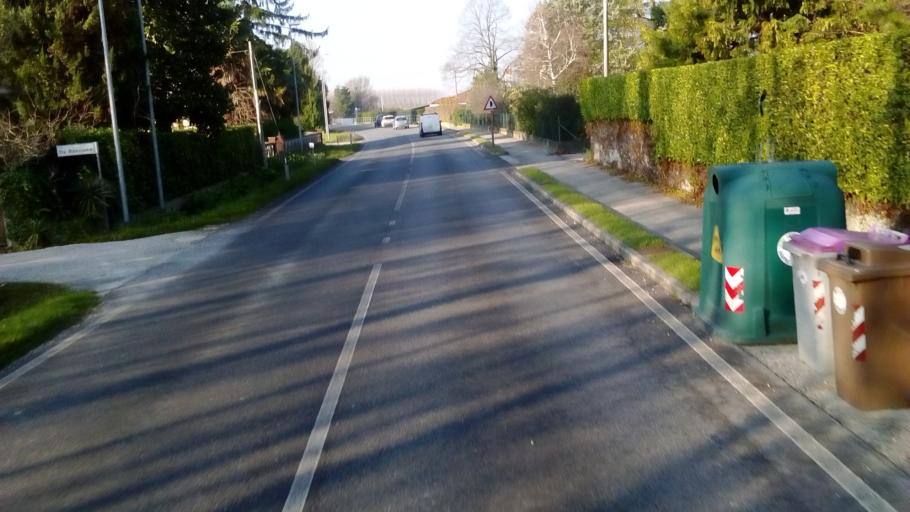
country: IT
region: Friuli Venezia Giulia
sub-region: Provincia di Udine
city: San Giorgio di Nogaro
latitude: 45.8348
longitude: 13.1926
